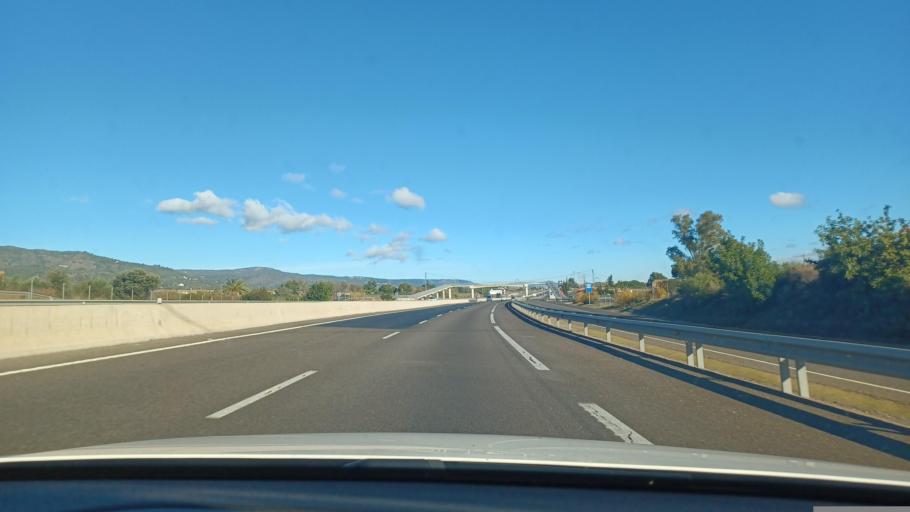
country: ES
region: Catalonia
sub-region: Provincia de Tarragona
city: Almoster
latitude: 41.1769
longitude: 1.1311
